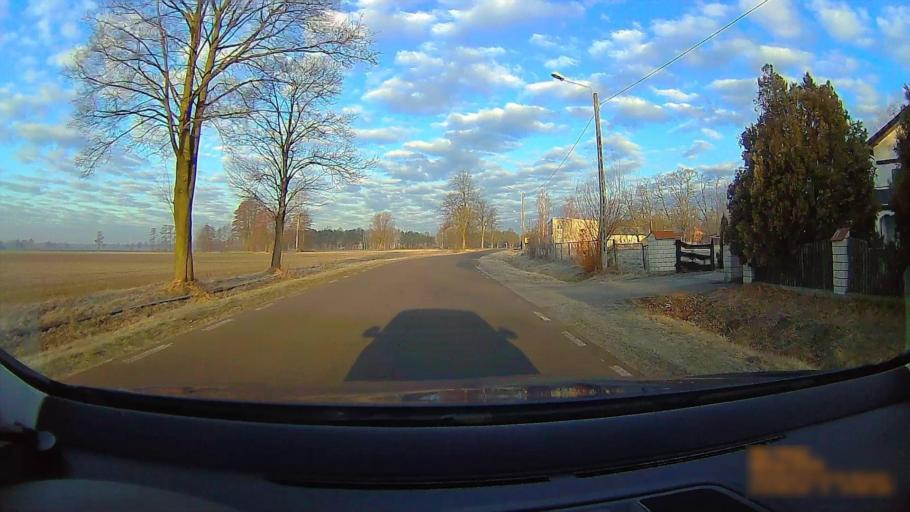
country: PL
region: Greater Poland Voivodeship
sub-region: Powiat koninski
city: Rychwal
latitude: 52.1003
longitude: 18.1002
